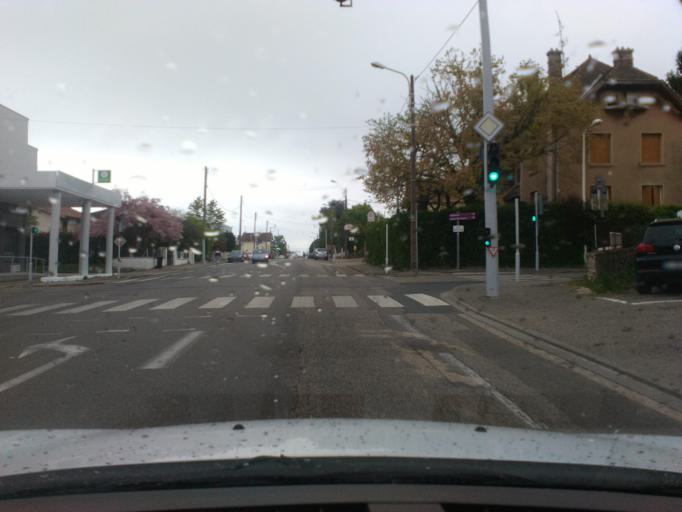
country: FR
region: Rhone-Alpes
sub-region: Departement de l'Ain
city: Peronnas
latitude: 46.1879
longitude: 5.2095
